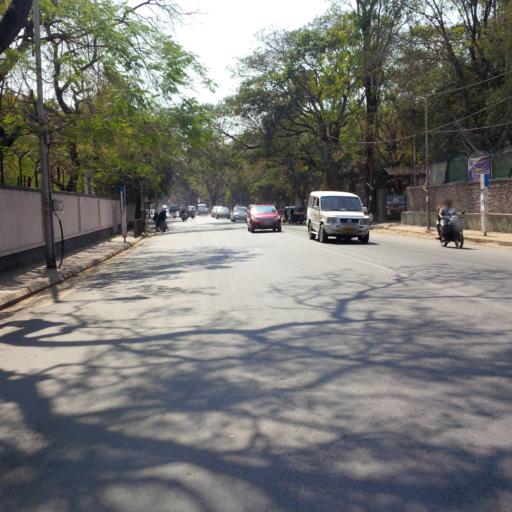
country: IN
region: Maharashtra
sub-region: Pune Division
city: Pune
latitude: 18.5176
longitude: 73.8298
